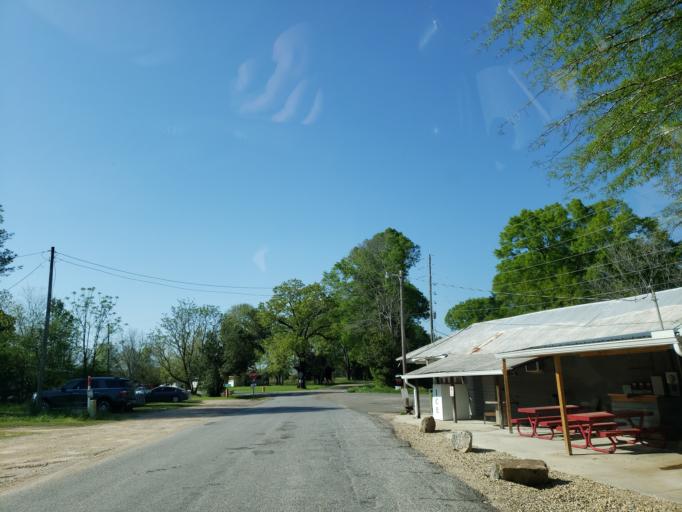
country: US
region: Mississippi
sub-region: Forrest County
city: Rawls Springs
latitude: 31.5404
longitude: -89.3648
